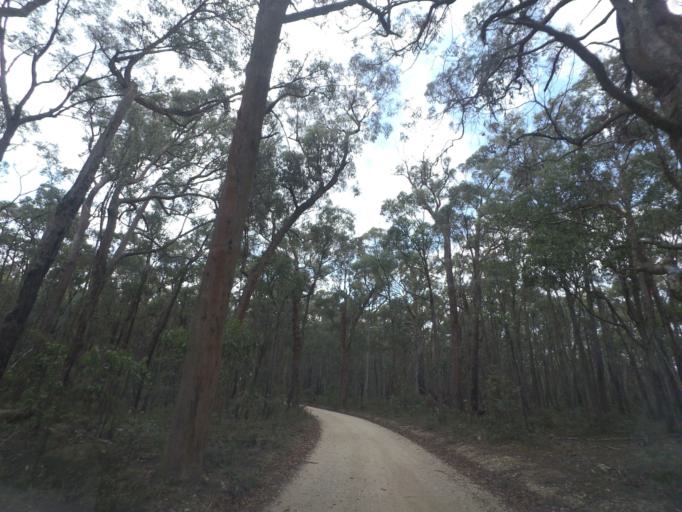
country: AU
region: Victoria
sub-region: Moorabool
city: Bacchus Marsh
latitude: -37.4965
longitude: 144.4339
